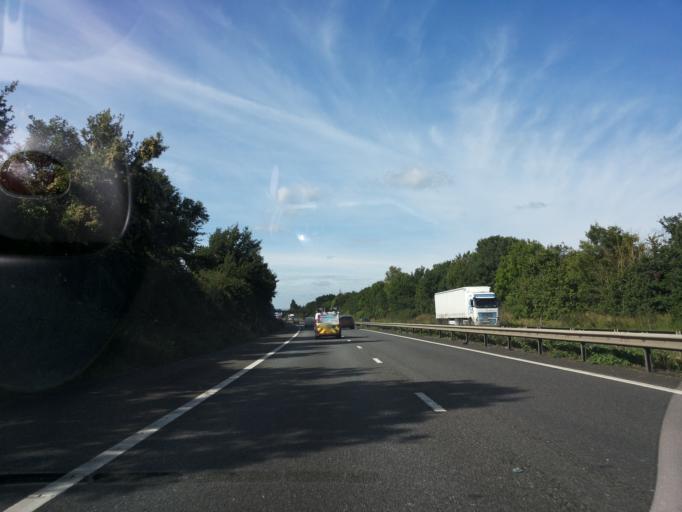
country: GB
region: England
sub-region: Kent
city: Newington
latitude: 51.3187
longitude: 0.6941
